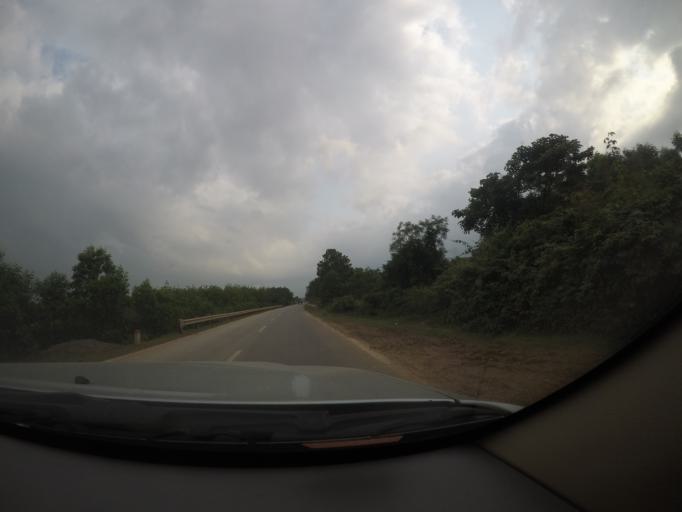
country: VN
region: Quang Tri
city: Ho Xa
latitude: 17.0656
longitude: 106.8608
